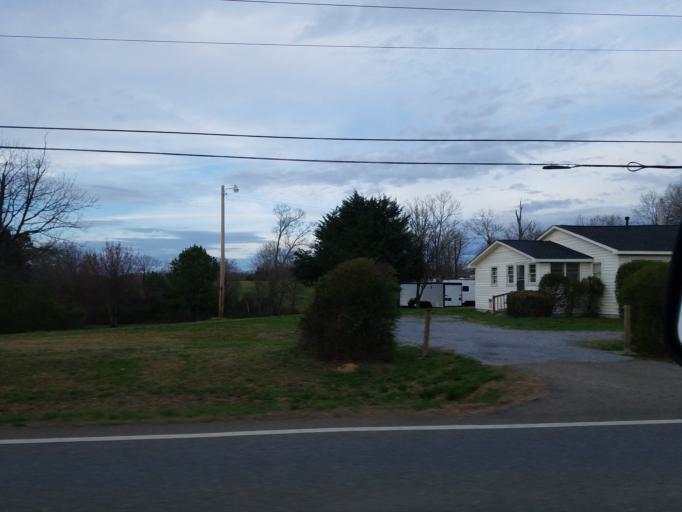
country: US
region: Georgia
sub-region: Gordon County
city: Calhoun
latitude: 34.4511
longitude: -84.8655
